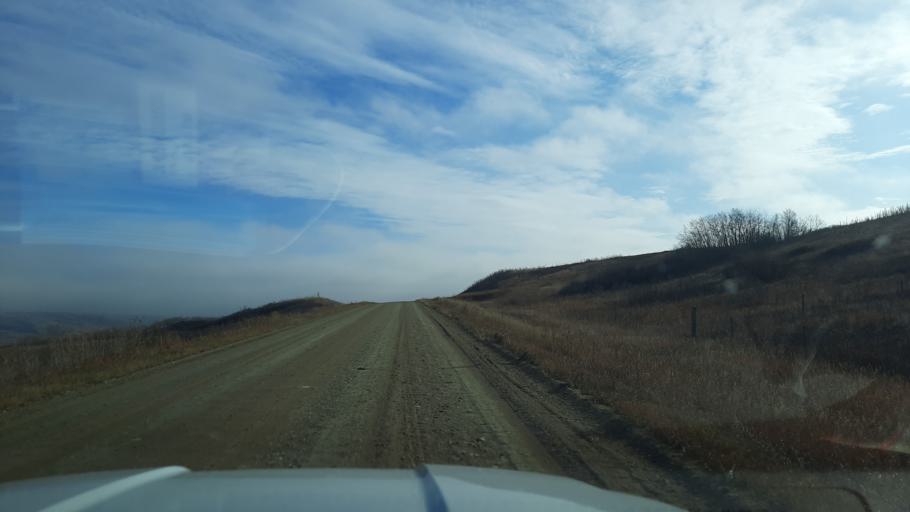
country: CA
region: Saskatchewan
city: Pilot Butte
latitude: 50.7840
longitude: -104.2273
